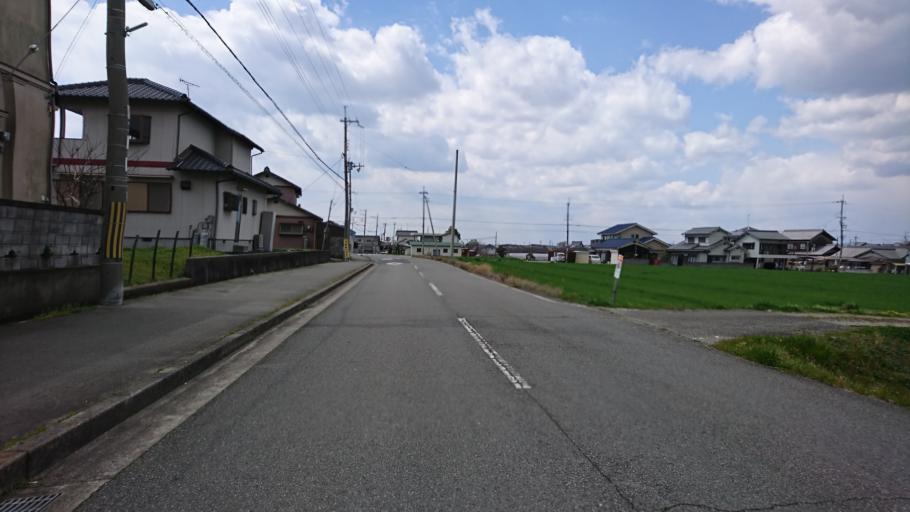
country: JP
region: Hyogo
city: Kakogawacho-honmachi
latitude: 34.7535
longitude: 134.9037
